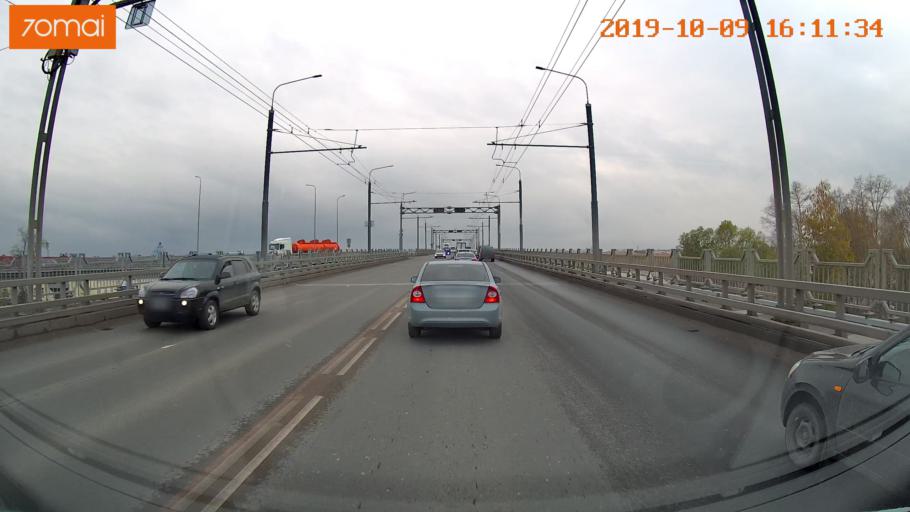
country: RU
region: Kostroma
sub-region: Kostromskoy Rayon
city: Kostroma
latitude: 57.7565
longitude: 40.9445
